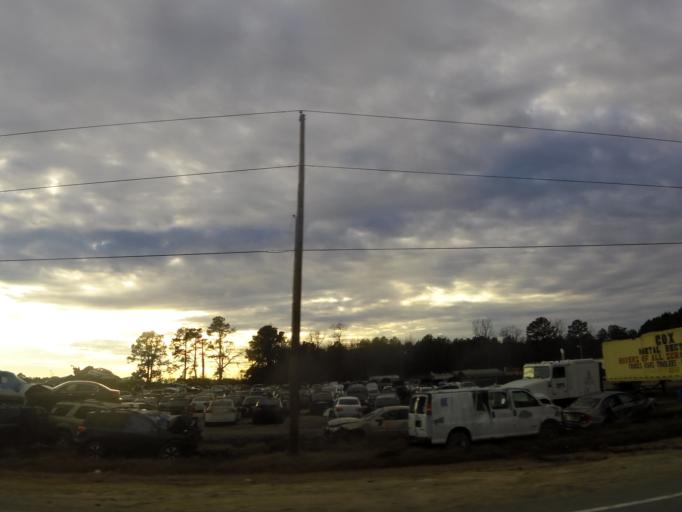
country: US
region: North Carolina
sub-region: Nash County
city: Sharpsburg
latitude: 35.8954
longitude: -77.8242
